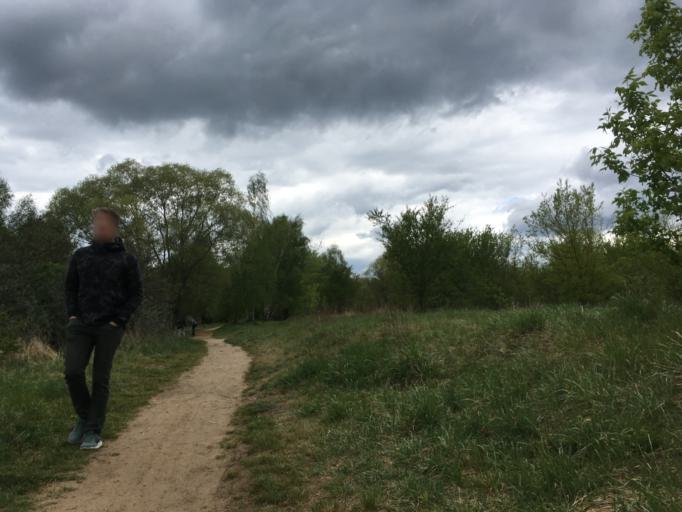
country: DE
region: Berlin
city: Blankenfelde
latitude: 52.6363
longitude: 13.4162
